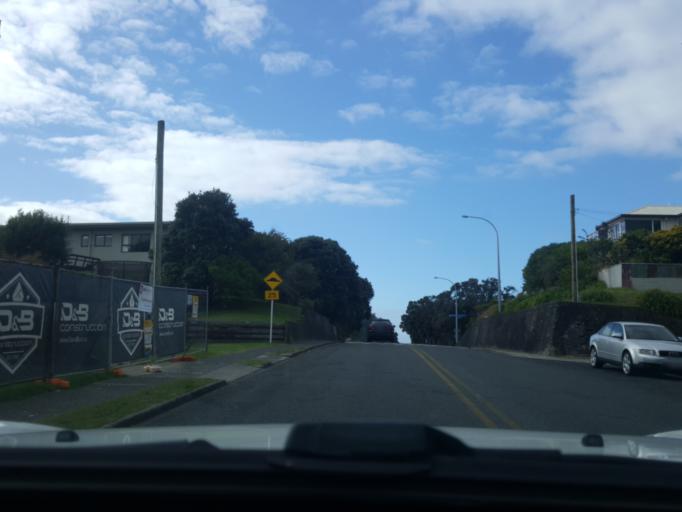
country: NZ
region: Bay of Plenty
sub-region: Tauranga City
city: Tauranga
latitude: -37.6387
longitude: 176.1854
